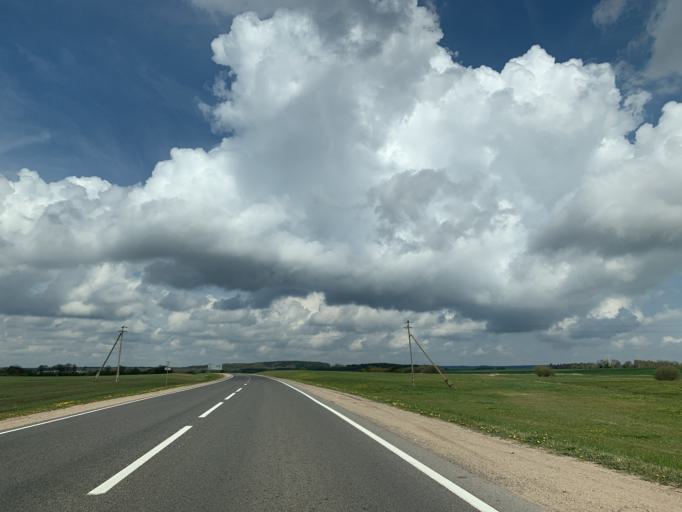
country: BY
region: Minsk
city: Nyasvizh
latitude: 53.2303
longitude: 26.7232
